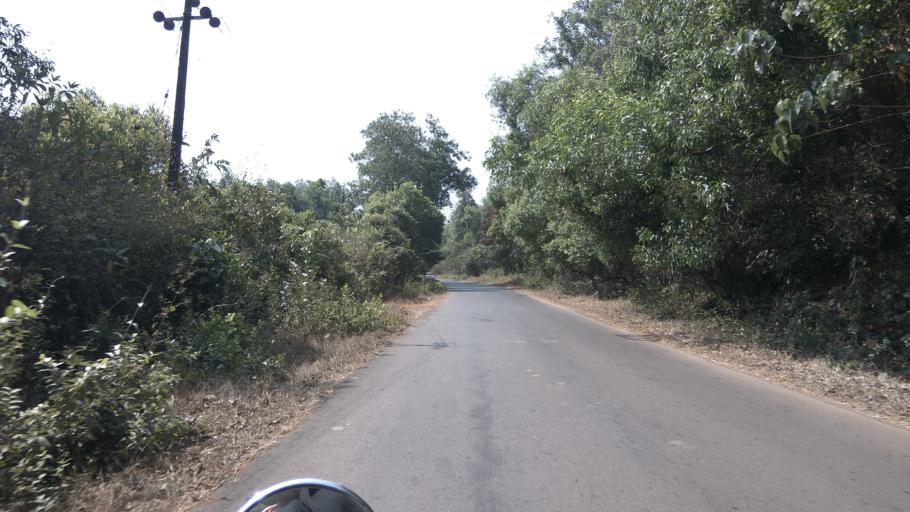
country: IN
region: Goa
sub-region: South Goa
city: Sanvordem
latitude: 15.3599
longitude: 74.2321
